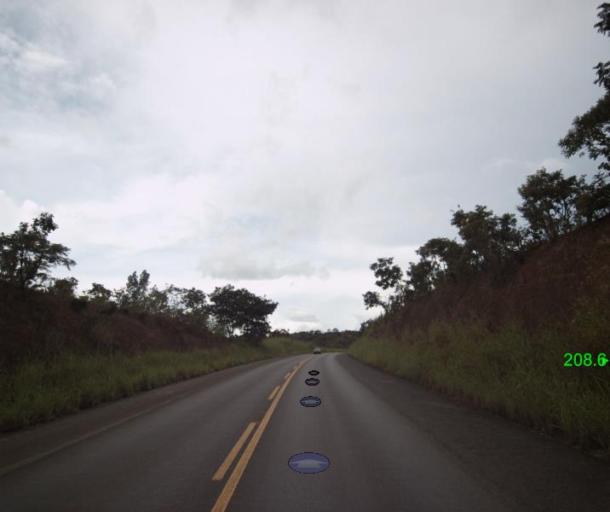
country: BR
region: Goias
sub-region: Niquelandia
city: Niquelandia
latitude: -14.4993
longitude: -48.5050
